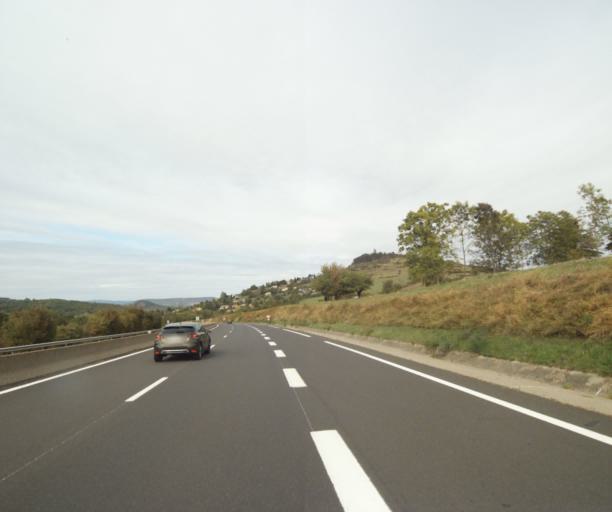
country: FR
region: Auvergne
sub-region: Departement du Puy-de-Dome
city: Ceyrat
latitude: 45.7220
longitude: 3.0716
